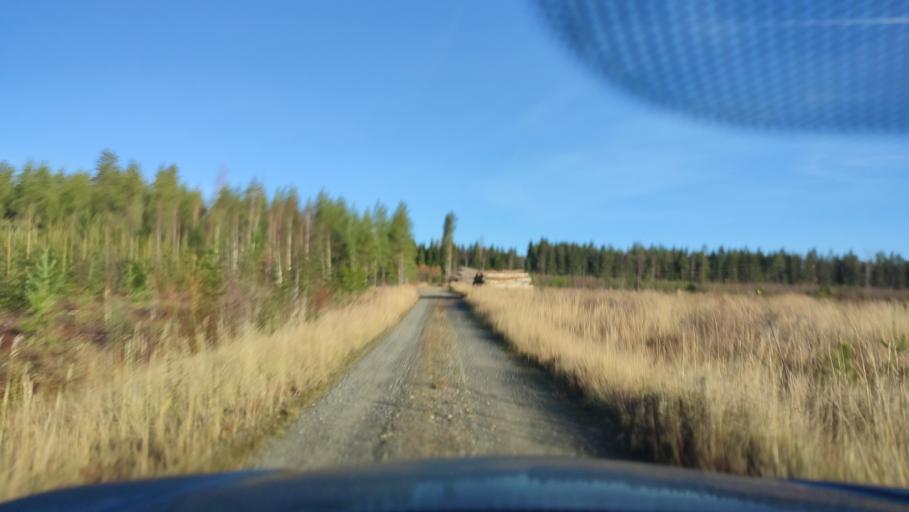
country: FI
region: Southern Ostrobothnia
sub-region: Suupohja
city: Karijoki
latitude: 62.2014
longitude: 21.6143
